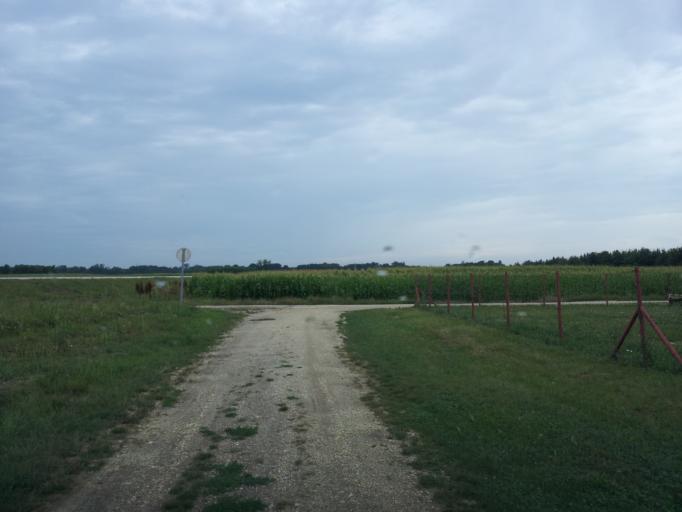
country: HU
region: Vas
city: Kormend
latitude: 46.9549
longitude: 16.6439
